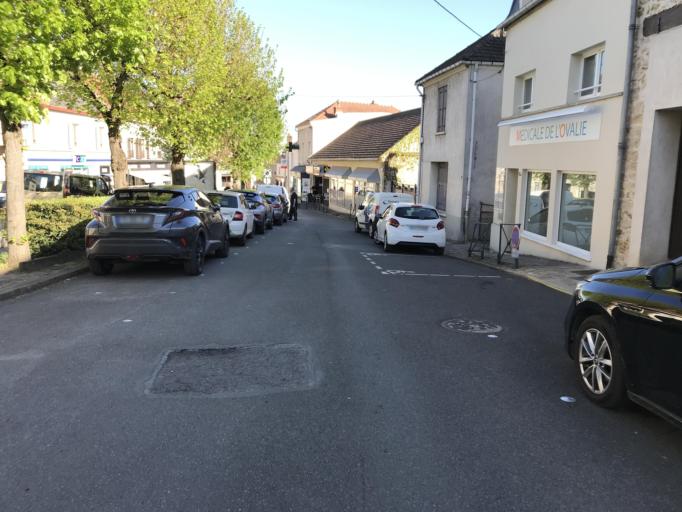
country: FR
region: Ile-de-France
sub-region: Departement de l'Essonne
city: Marcoussis
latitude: 48.6429
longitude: 2.2284
